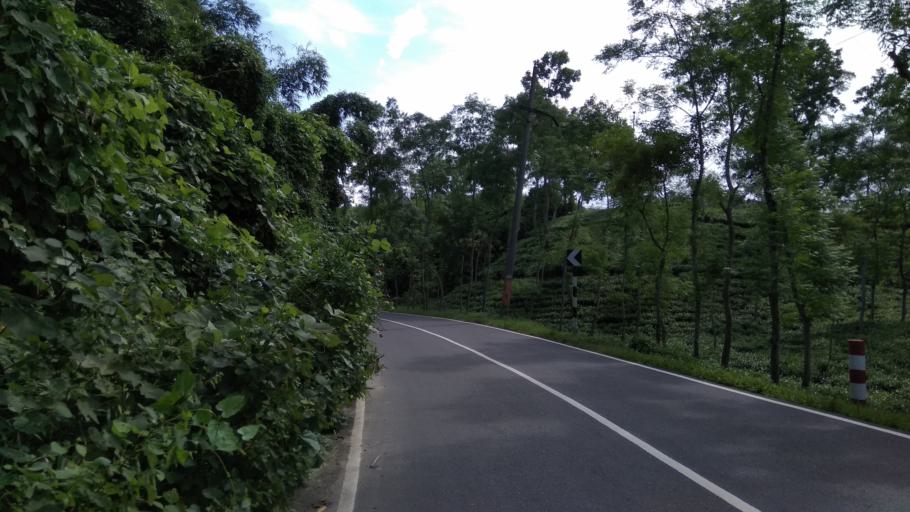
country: IN
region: Tripura
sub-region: Dhalai
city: Kamalpur
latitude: 24.3065
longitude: 91.7699
